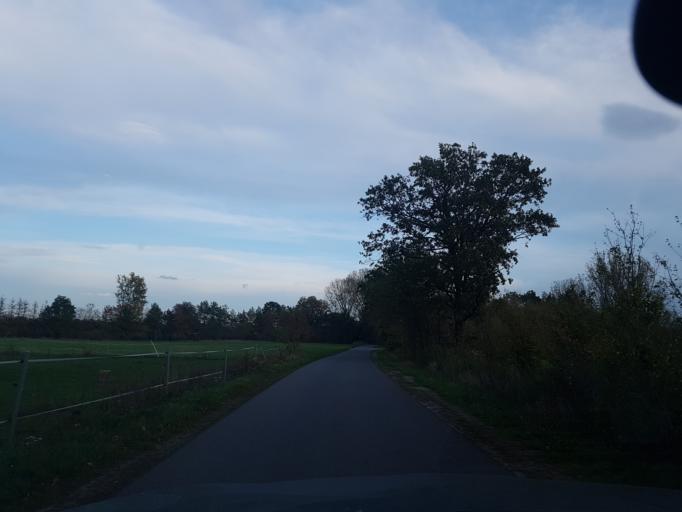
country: DE
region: Saxony
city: Nauwalde
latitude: 51.4594
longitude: 13.4508
